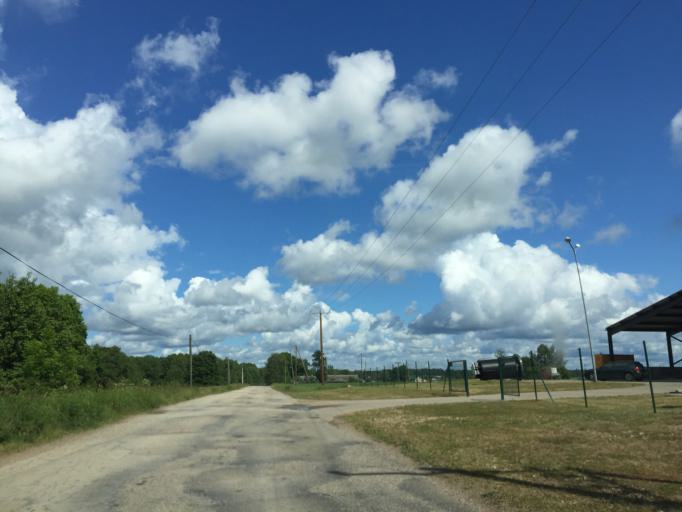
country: LV
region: Lecava
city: Iecava
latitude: 56.6083
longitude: 24.1915
